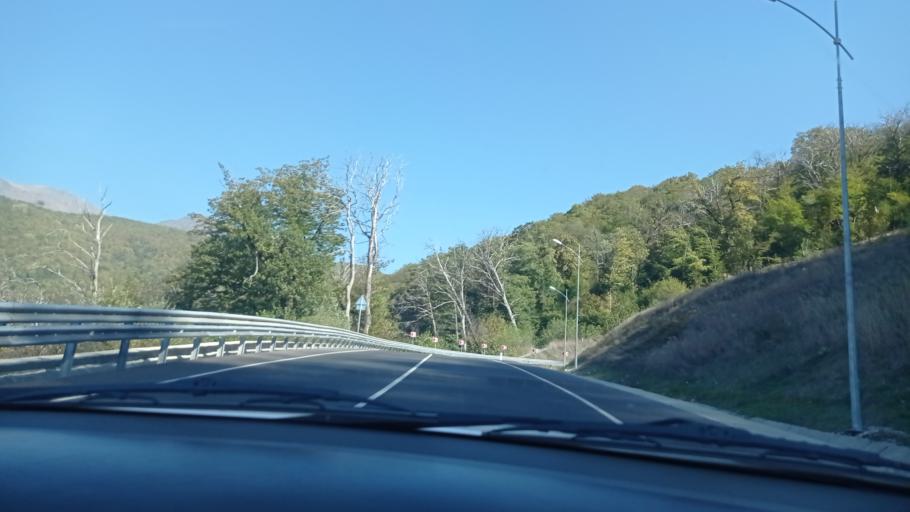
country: RU
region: Krasnodarskiy
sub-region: Sochi City
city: Krasnaya Polyana
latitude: 43.6816
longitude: 40.2450
